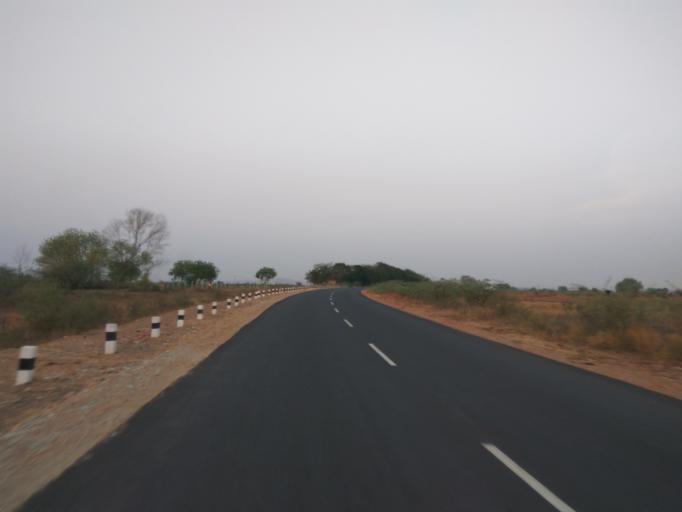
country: IN
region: Andhra Pradesh
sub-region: Prakasam
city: Markapur
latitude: 15.7499
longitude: 79.2178
